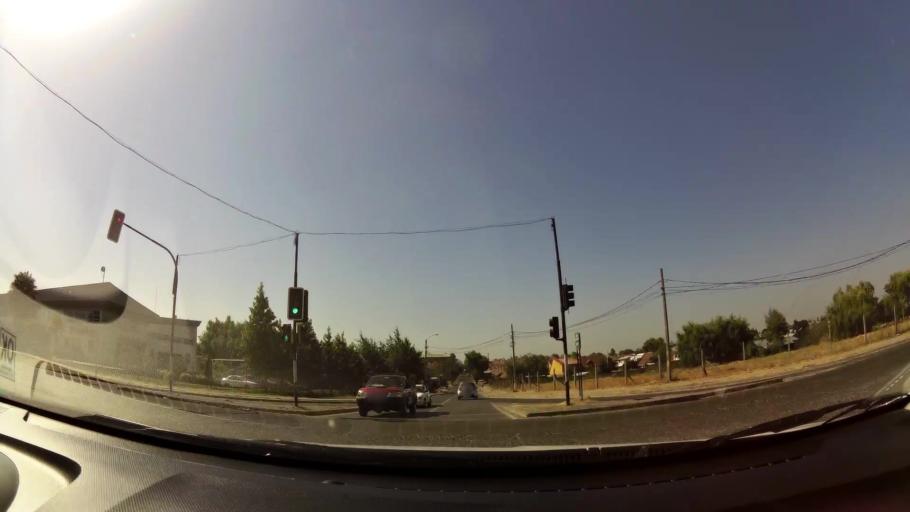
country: CL
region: Maule
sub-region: Provincia de Talca
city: Talca
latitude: -35.4067
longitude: -71.6453
